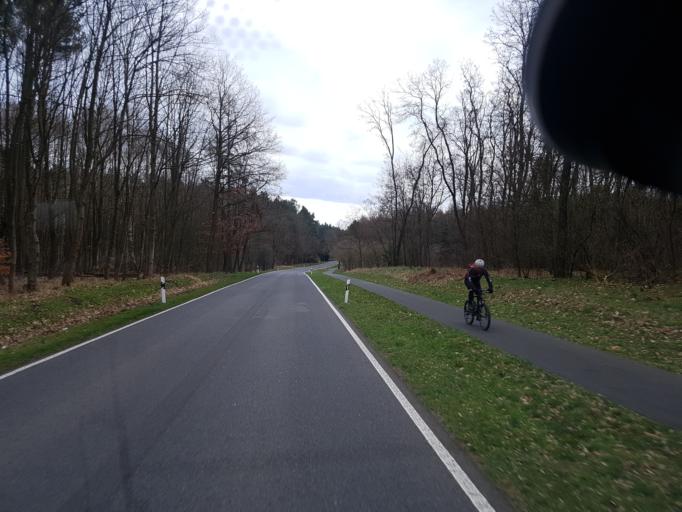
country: DE
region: Brandenburg
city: Gross Lindow
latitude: 52.1669
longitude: 14.4990
